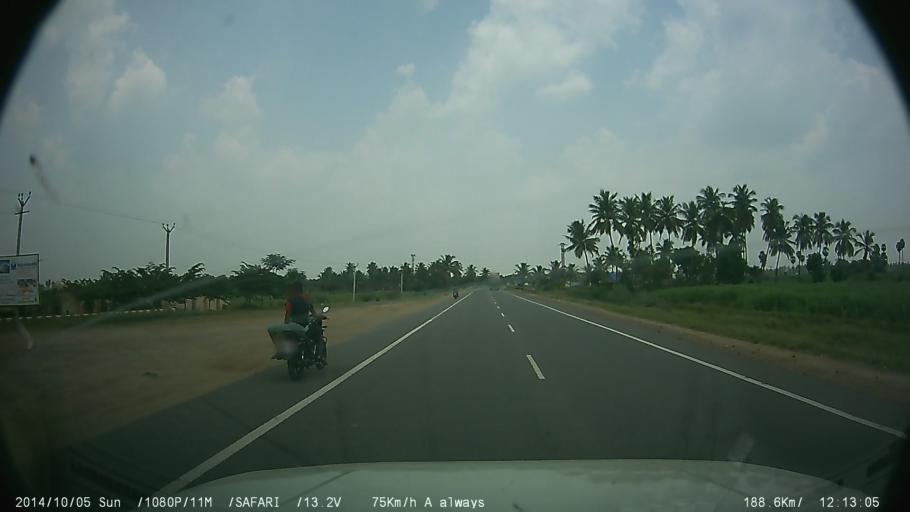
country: IN
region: Tamil Nadu
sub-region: Villupuram
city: Kallakkurichchi
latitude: 11.7287
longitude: 78.9768
